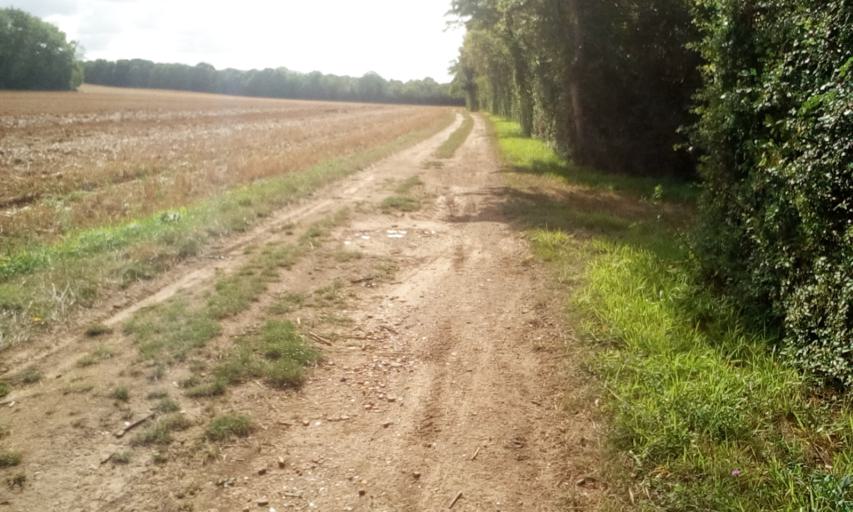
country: FR
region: Lower Normandy
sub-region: Departement du Calvados
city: Cagny
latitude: 49.1044
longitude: -0.2492
